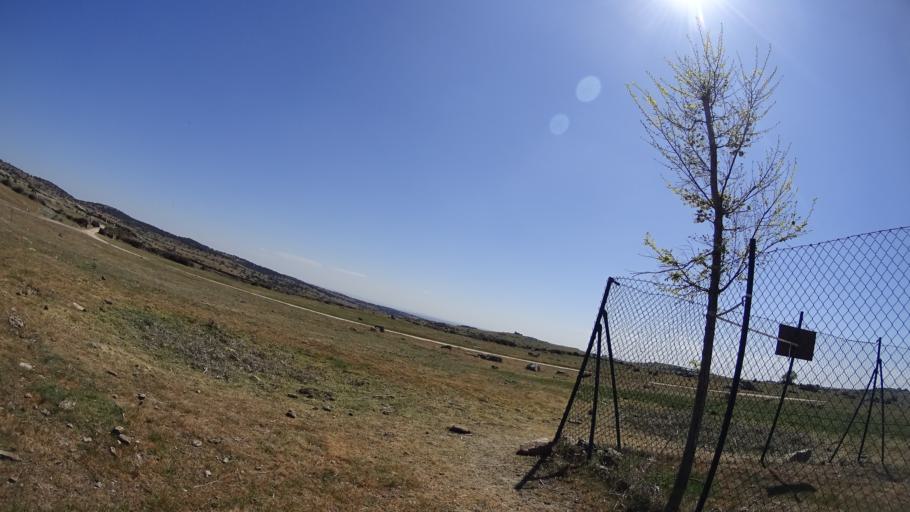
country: ES
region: Madrid
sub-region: Provincia de Madrid
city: Colmenar Viejo
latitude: 40.7000
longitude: -3.7513
